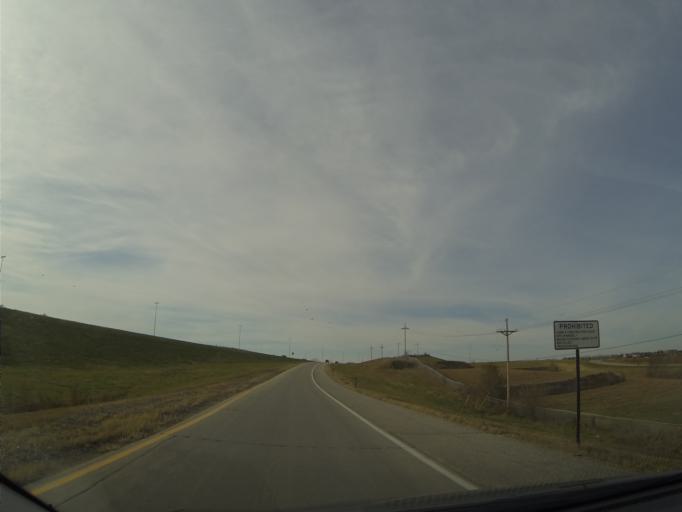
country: US
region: Nebraska
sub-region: Douglas County
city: Elkhorn
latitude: 41.2639
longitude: -96.2162
